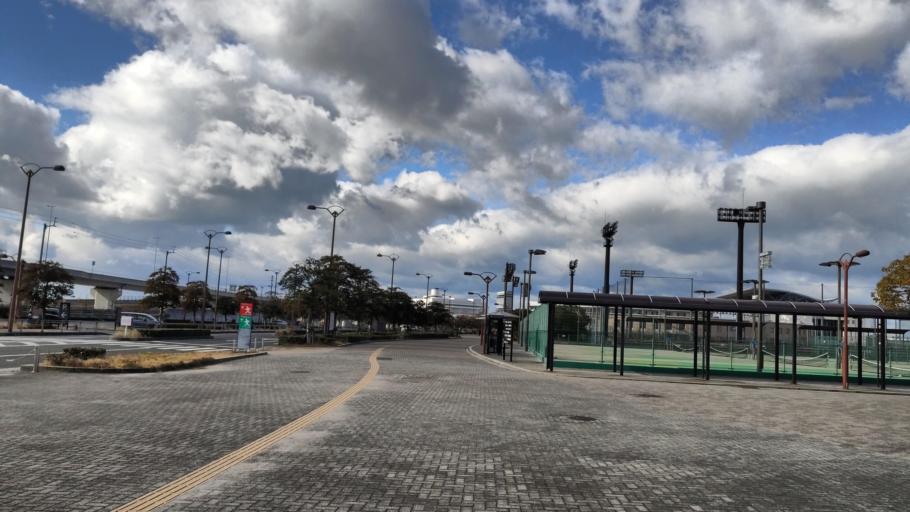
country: JP
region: Ehime
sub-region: Shikoku-chuo Shi
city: Matsuyama
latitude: 33.8076
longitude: 132.7463
